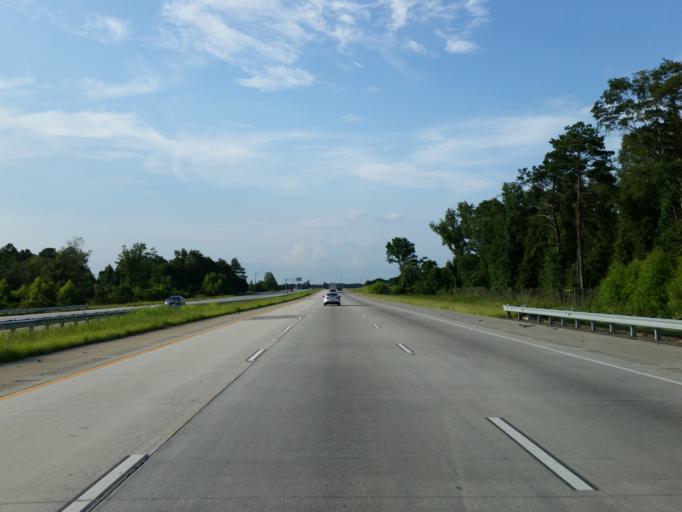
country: US
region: Georgia
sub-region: Dooly County
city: Unadilla
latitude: 32.2048
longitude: -83.7462
